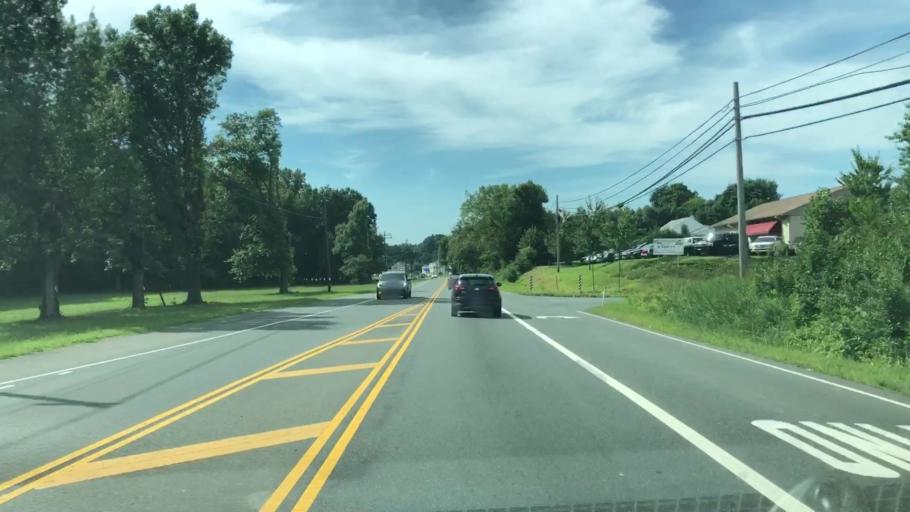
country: US
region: Virginia
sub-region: City of Fredericksburg
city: Fredericksburg
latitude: 38.2812
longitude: -77.4536
